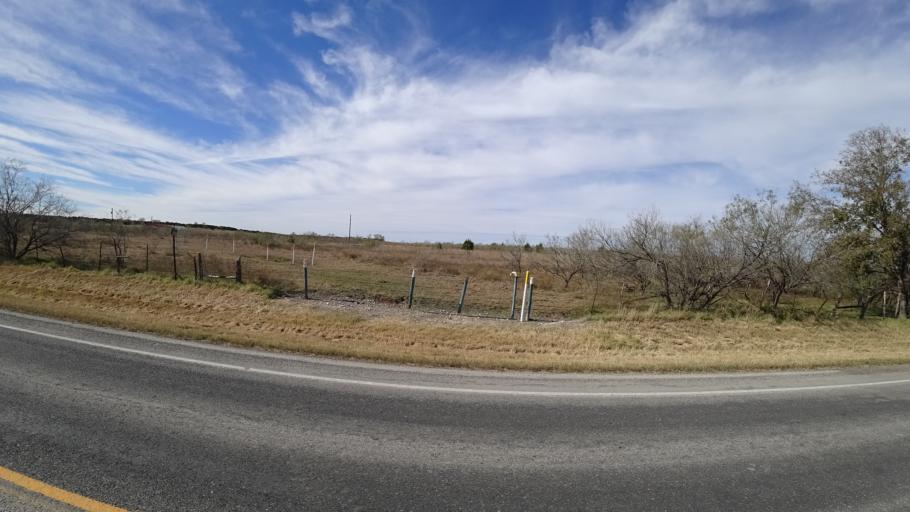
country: US
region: Texas
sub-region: Travis County
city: Onion Creek
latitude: 30.1120
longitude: -97.7207
